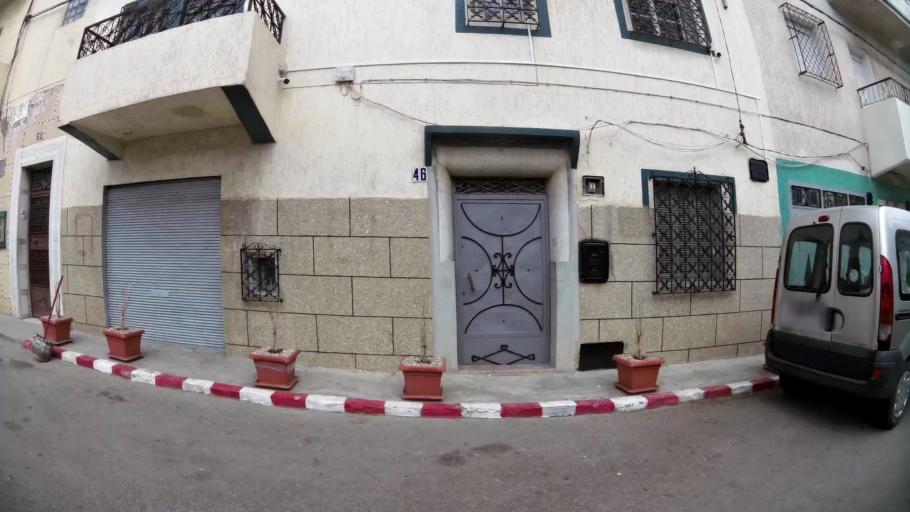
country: MA
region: Tanger-Tetouan
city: Tetouan
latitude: 35.5770
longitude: -5.3625
